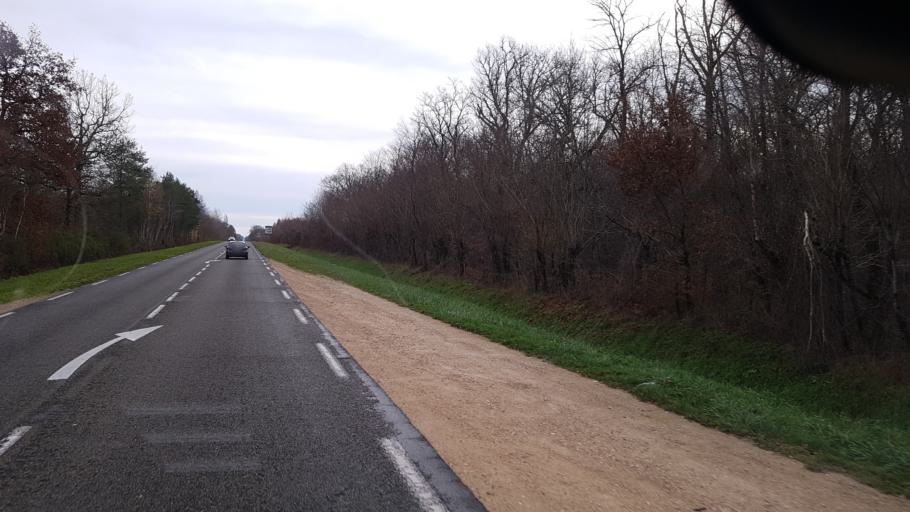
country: FR
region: Centre
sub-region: Departement du Loiret
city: La Ferte-Saint-Aubin
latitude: 47.6931
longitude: 1.9548
